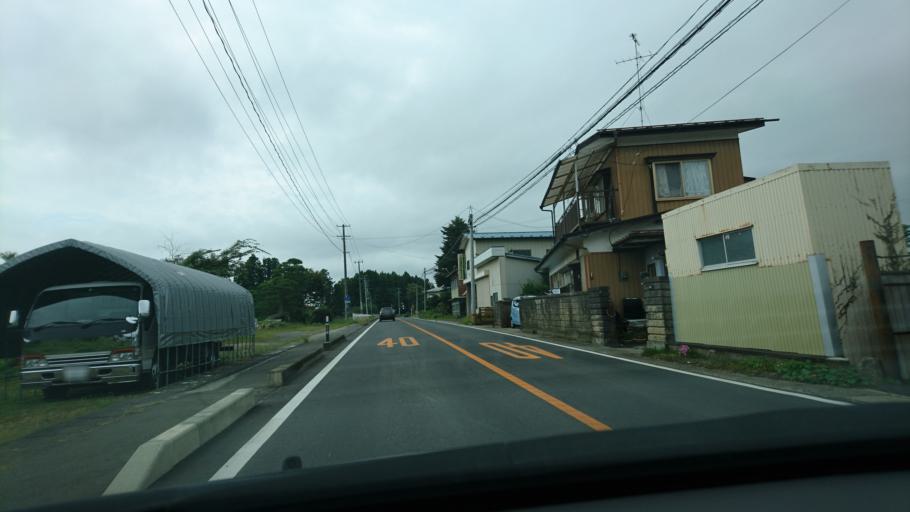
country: JP
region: Iwate
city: Ichinoseki
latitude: 38.7684
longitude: 141.0928
